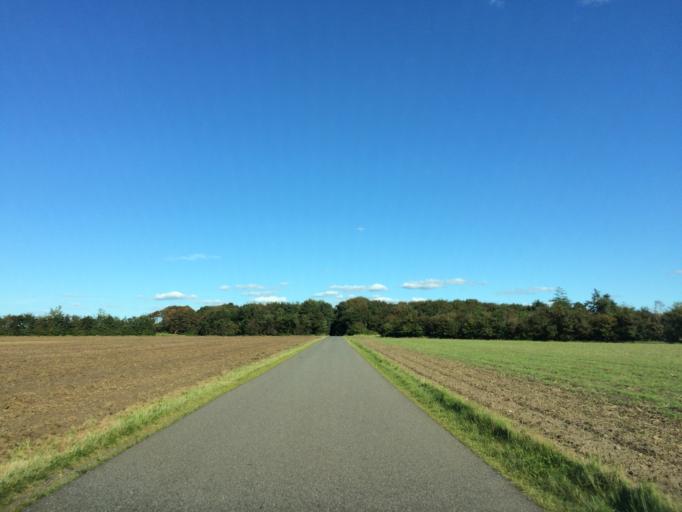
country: DK
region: Central Jutland
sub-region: Holstebro Kommune
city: Holstebro
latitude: 56.2638
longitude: 8.5513
